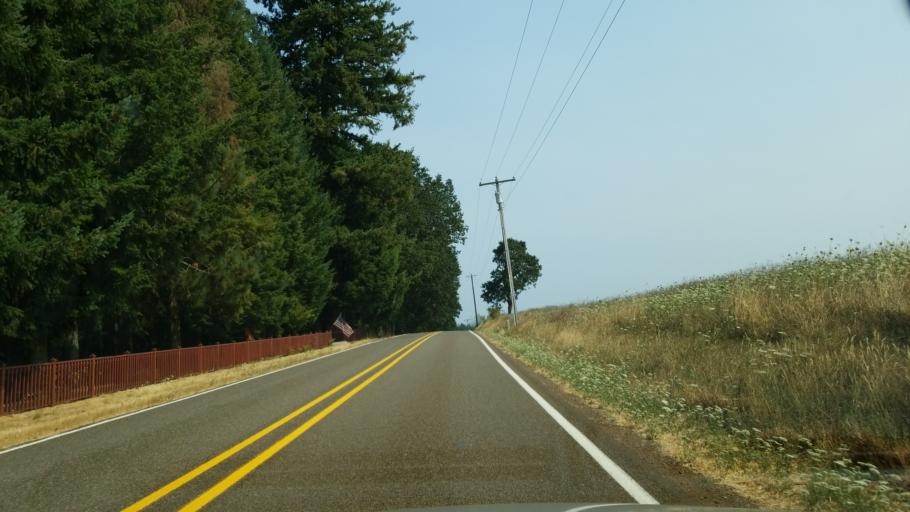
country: US
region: Oregon
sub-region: Marion County
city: Aumsville
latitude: 44.9166
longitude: -122.8274
